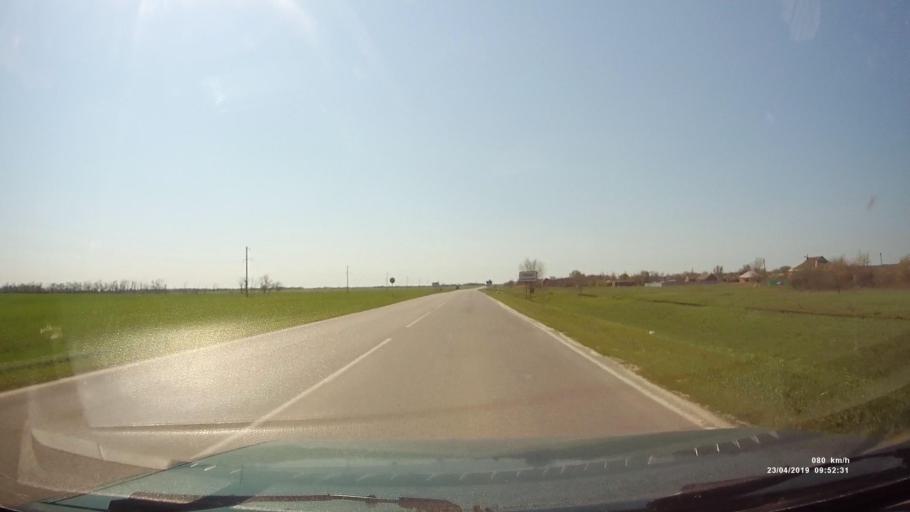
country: RU
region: Rostov
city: Orlovskiy
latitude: 46.8437
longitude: 42.0462
